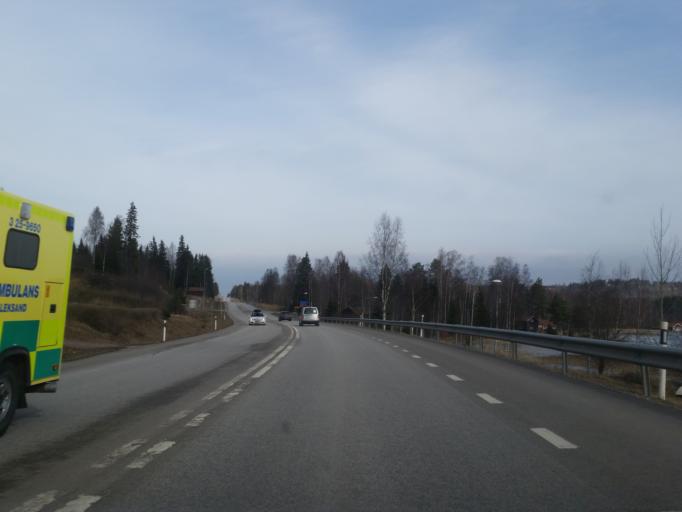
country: SE
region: Dalarna
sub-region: Leksand Municipality
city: Leksand
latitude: 60.7962
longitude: 15.0518
